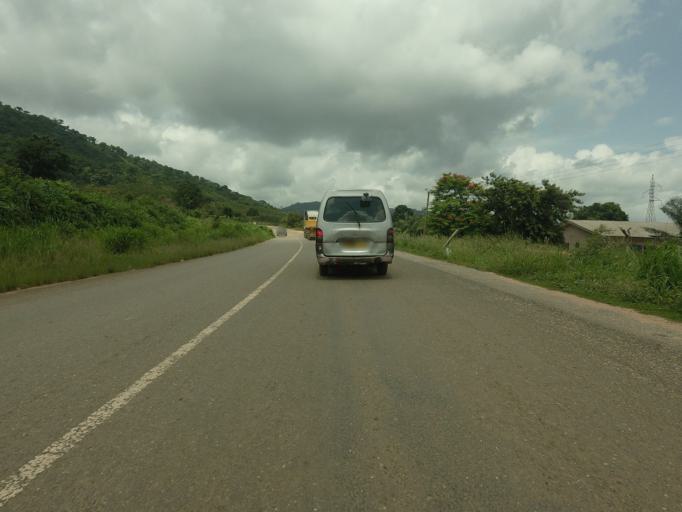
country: GH
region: Volta
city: Ho
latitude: 6.7047
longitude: 0.3342
